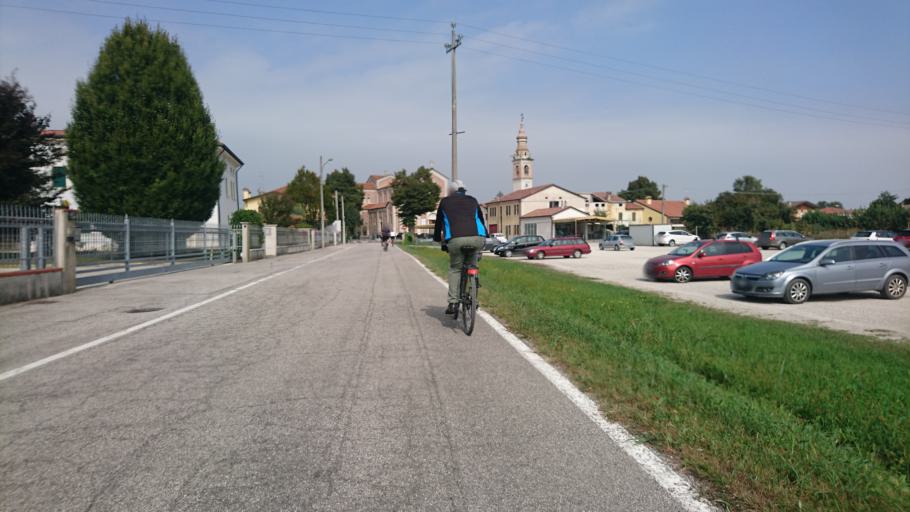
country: IT
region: Veneto
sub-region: Provincia di Padova
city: Grantorto
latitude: 45.5860
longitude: 11.7463
